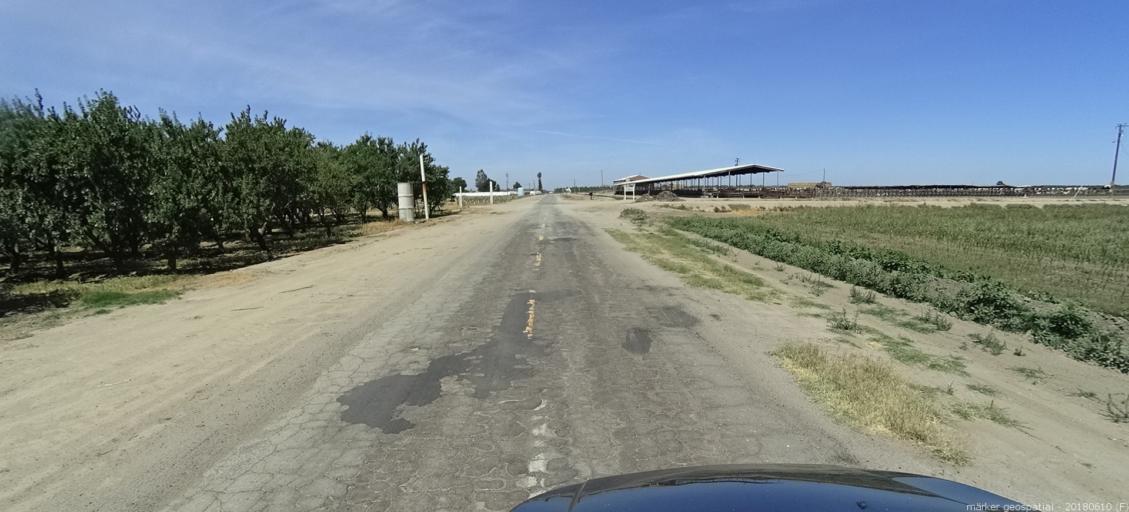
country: US
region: California
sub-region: Madera County
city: Chowchilla
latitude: 37.0398
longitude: -120.3730
